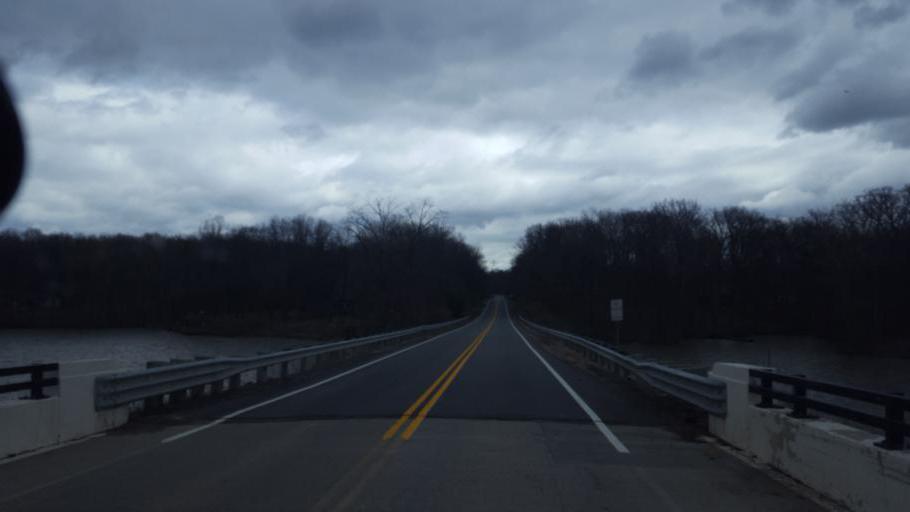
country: US
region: Ohio
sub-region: Delaware County
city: Sunbury
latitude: 40.1775
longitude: -82.8709
